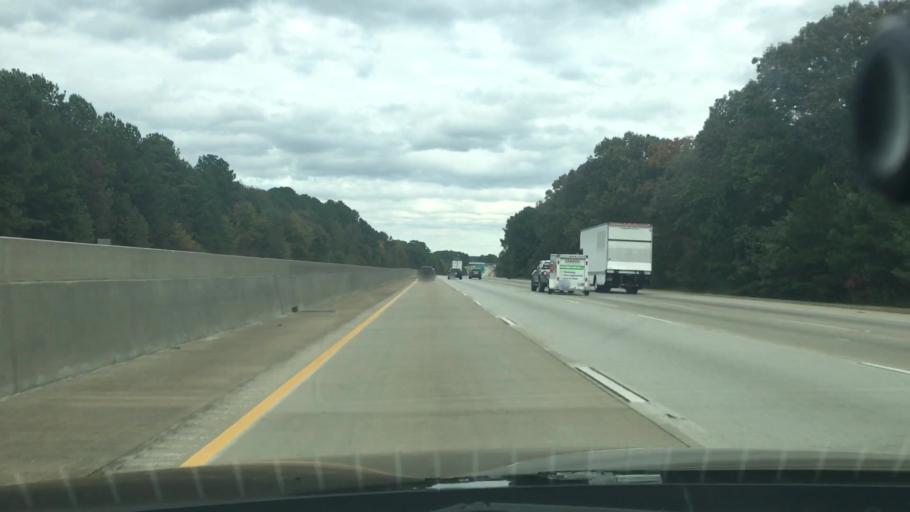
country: US
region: Georgia
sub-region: Fulton County
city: Palmetto
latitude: 33.4874
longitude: -84.6514
